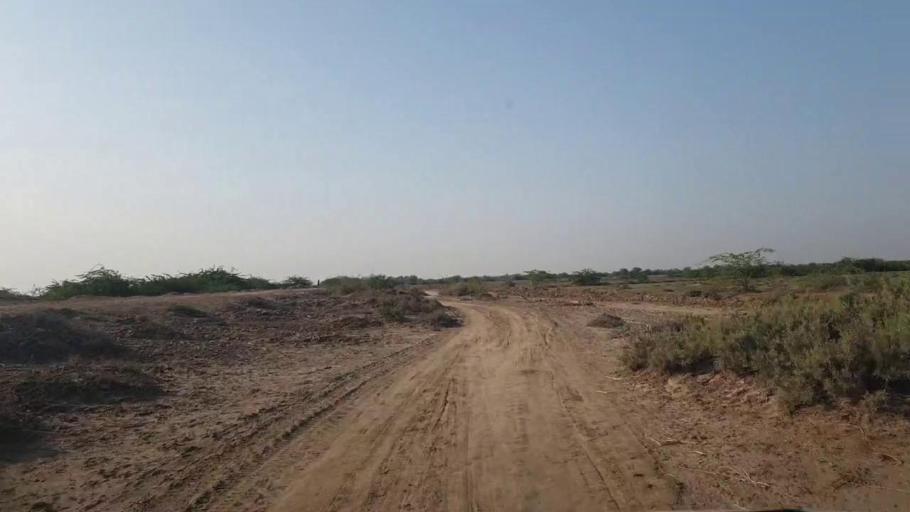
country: PK
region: Sindh
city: Badin
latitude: 24.4632
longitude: 68.7373
